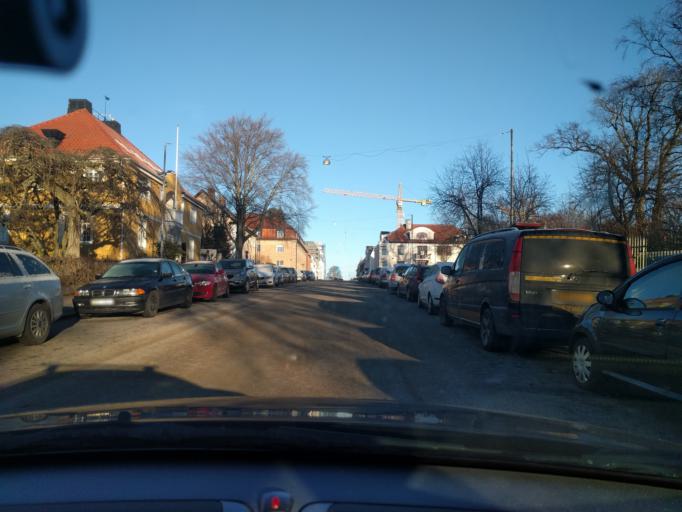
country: SE
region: Kronoberg
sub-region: Vaxjo Kommun
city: Vaexjoe
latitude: 56.8736
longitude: 14.8026
